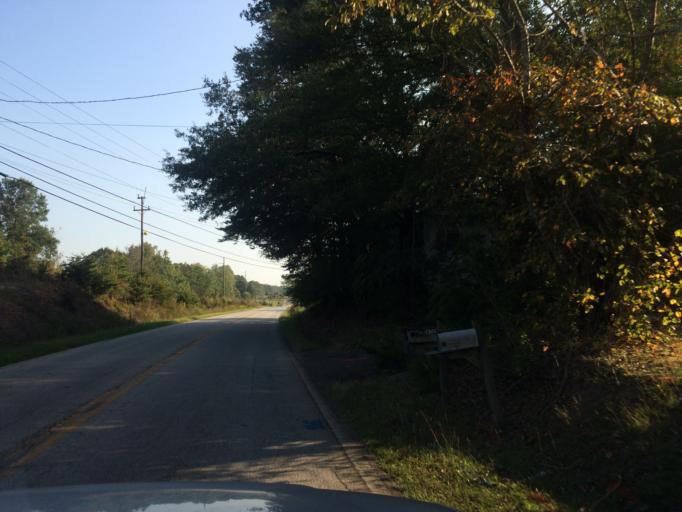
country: US
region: South Carolina
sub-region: Anderson County
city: Piedmont
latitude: 34.6869
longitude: -82.4509
